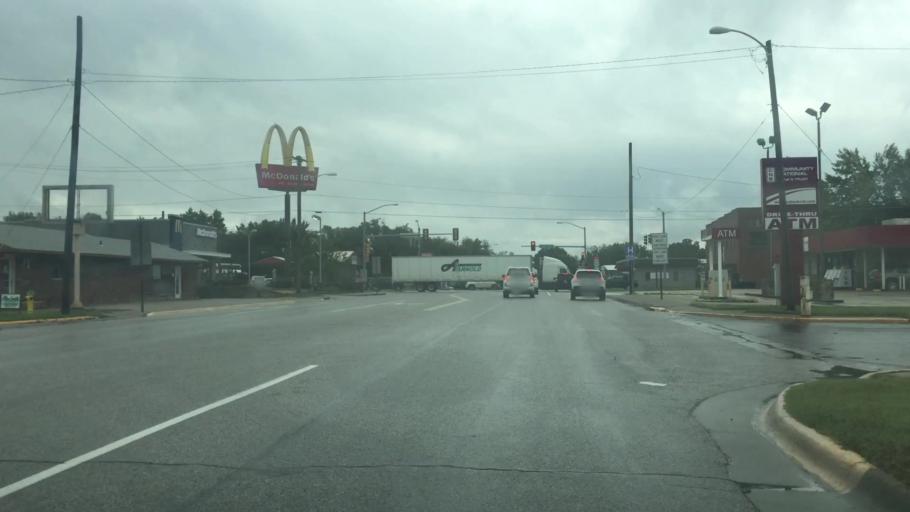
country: US
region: Kansas
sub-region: Allen County
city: Iola
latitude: 37.9224
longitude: -95.4091
